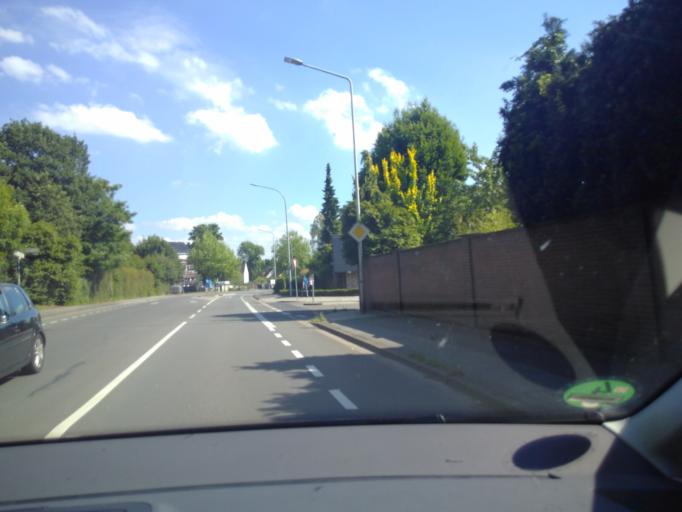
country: DE
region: North Rhine-Westphalia
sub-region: Regierungsbezirk Dusseldorf
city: Hilden
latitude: 51.1834
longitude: 6.9392
